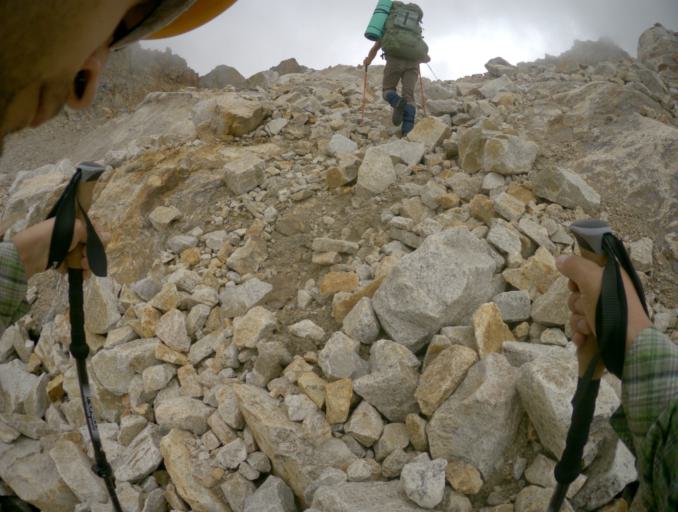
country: RU
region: Karachayevo-Cherkesiya
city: Uchkulan
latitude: 43.2793
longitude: 42.1124
